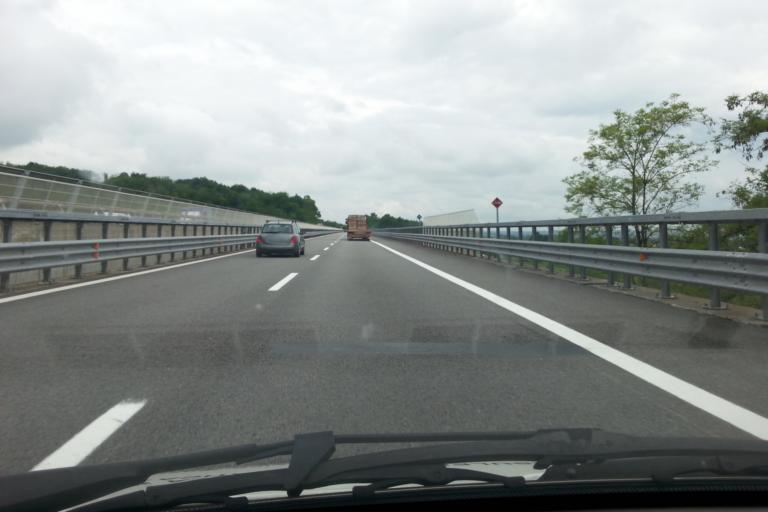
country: IT
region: Piedmont
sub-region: Provincia di Cuneo
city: Niella Tanaro
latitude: 44.4090
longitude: 7.9152
